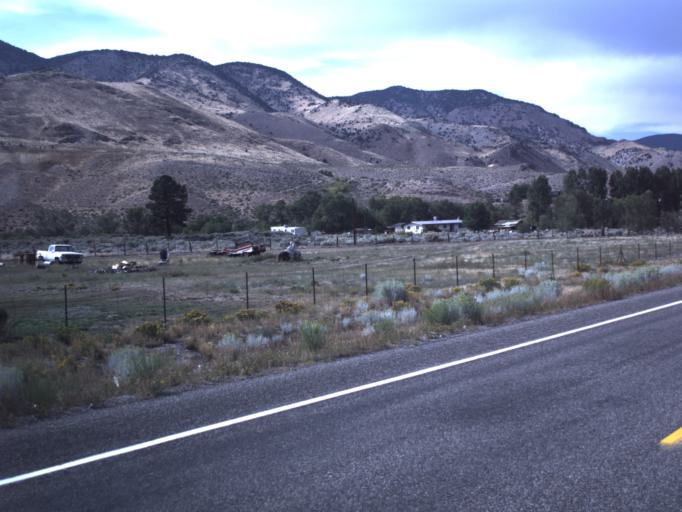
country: US
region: Utah
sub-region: Sevier County
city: Monroe
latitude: 38.4696
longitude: -112.2357
